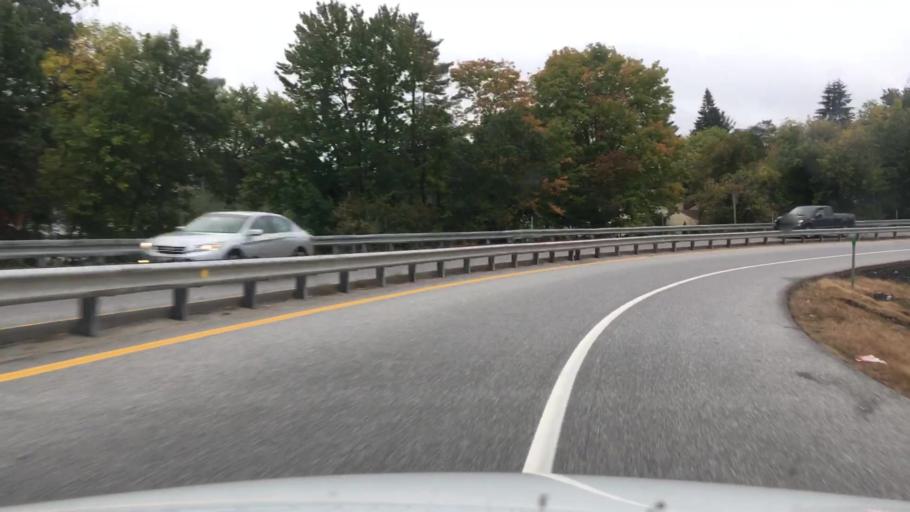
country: US
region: Maine
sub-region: Cumberland County
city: South Portland Gardens
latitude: 43.6799
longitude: -70.3236
